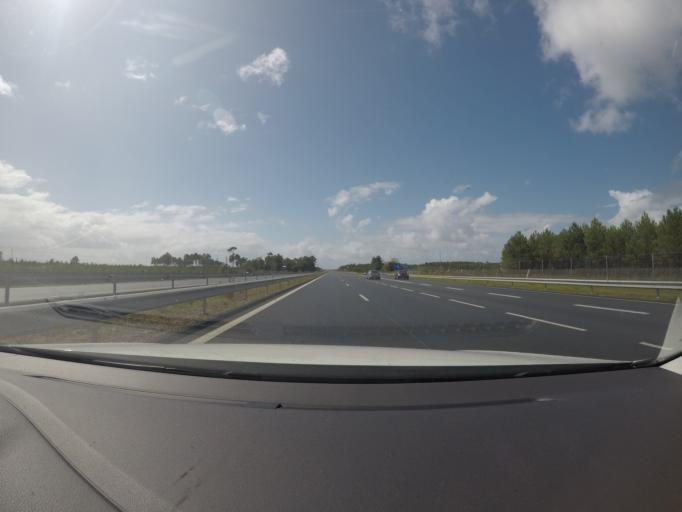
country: FR
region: Aquitaine
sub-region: Departement des Landes
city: Castets
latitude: 43.9410
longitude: -1.0861
